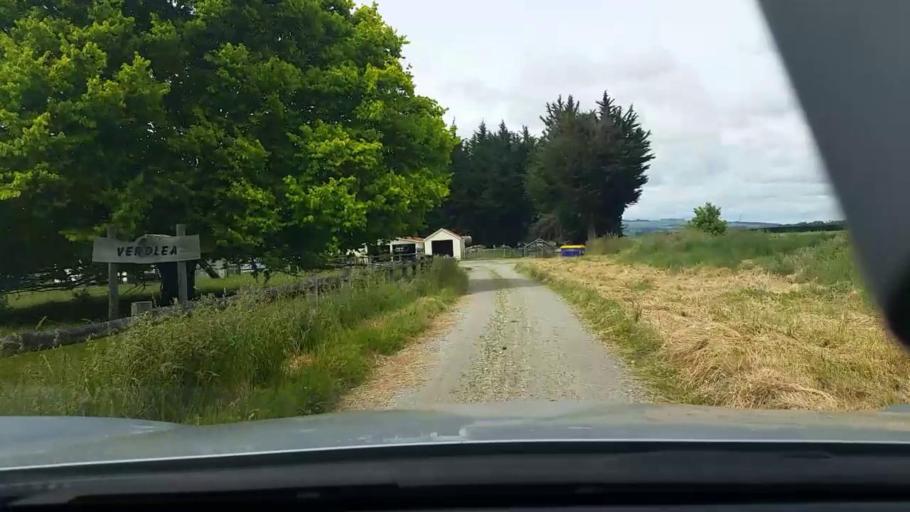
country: NZ
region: Southland
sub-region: Gore District
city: Gore
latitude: -46.1245
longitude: 168.9316
